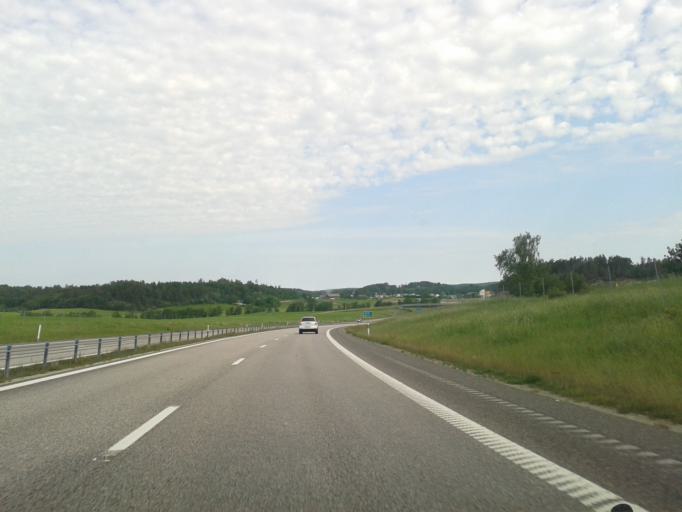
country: SE
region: Vaestra Goetaland
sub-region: Munkedals Kommun
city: Munkedal
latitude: 58.4770
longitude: 11.6370
